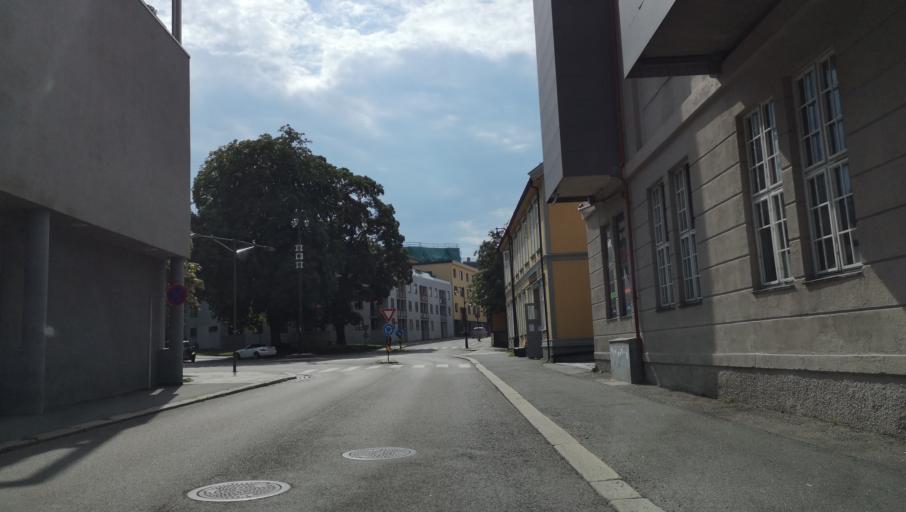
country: NO
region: Ostfold
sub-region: Moss
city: Moss
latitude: 59.4367
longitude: 10.6611
